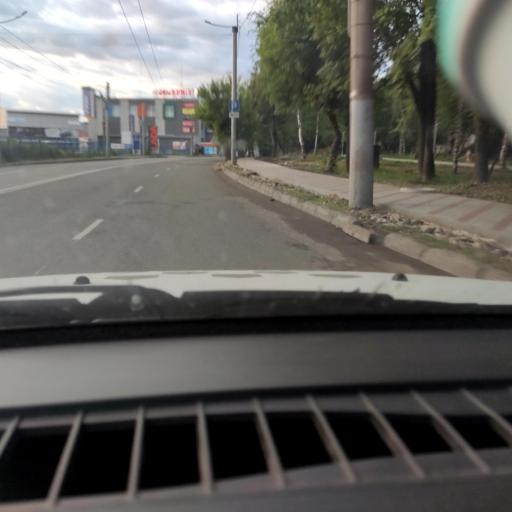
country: RU
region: Kirov
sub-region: Kirovo-Chepetskiy Rayon
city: Kirov
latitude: 58.6193
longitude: 49.6599
